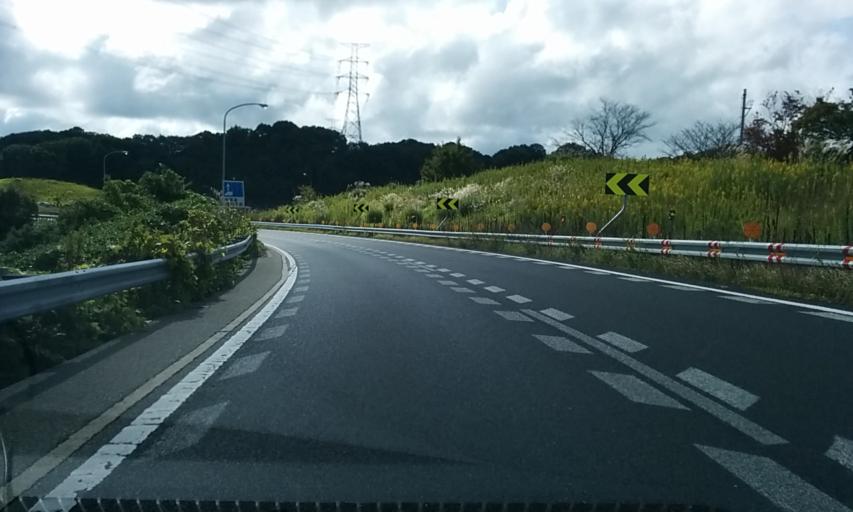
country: JP
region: Hyogo
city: Sandacho
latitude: 34.8947
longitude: 135.1519
